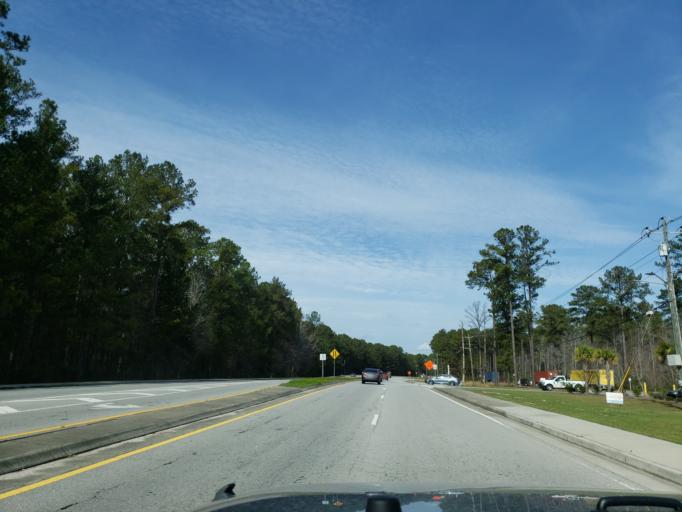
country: US
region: Georgia
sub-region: Chatham County
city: Pooler
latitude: 32.1644
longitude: -81.2332
